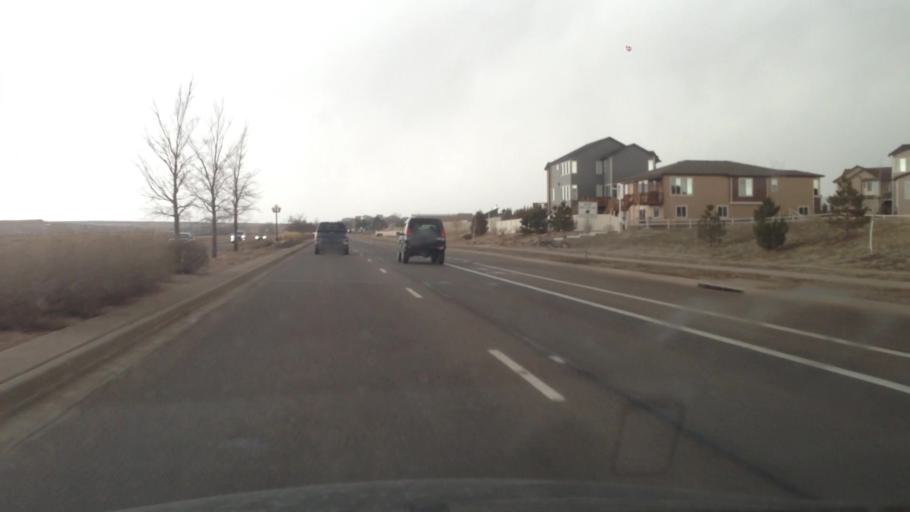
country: US
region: Colorado
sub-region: Douglas County
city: Parker
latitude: 39.4931
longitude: -104.7807
